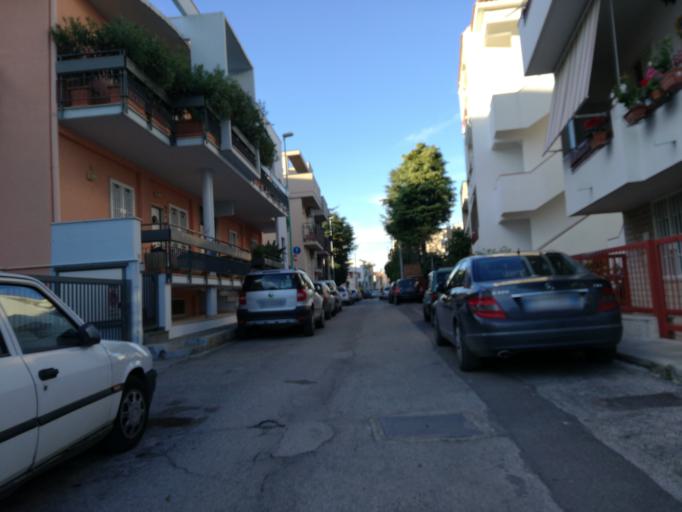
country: IT
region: Apulia
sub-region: Provincia di Bari
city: Adelfia
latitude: 41.0009
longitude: 16.8703
